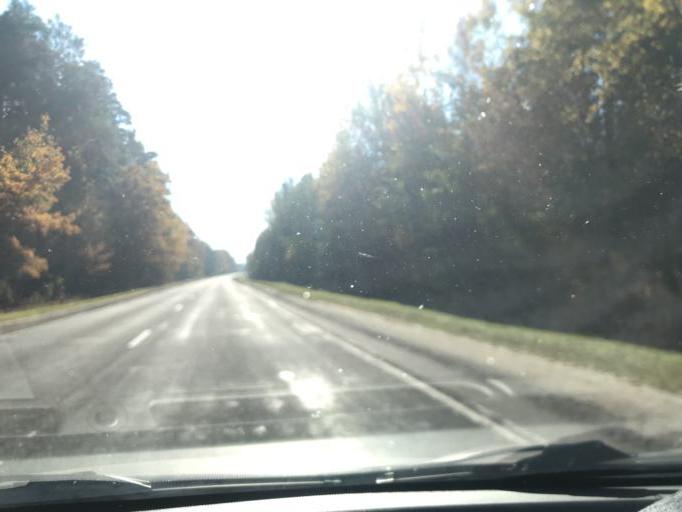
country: BY
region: Gomel
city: Gomel
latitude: 52.4042
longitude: 30.8290
